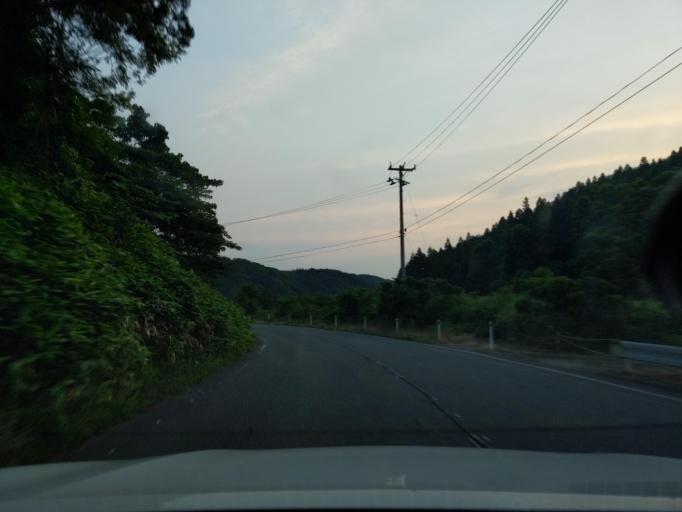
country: JP
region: Niigata
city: Kashiwazaki
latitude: 37.4537
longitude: 138.6291
